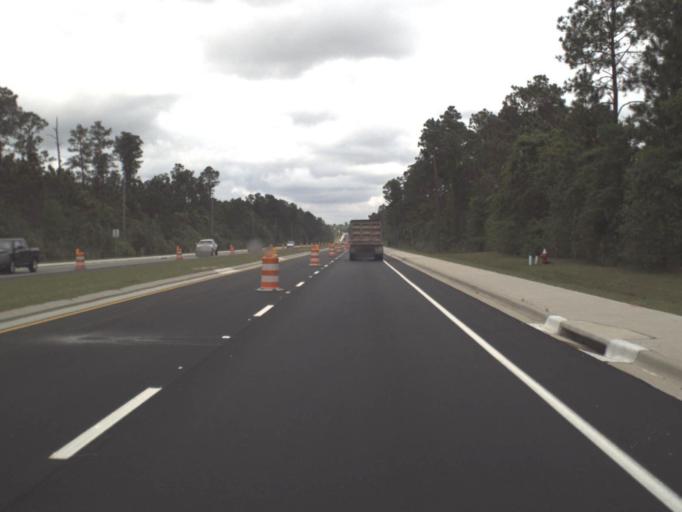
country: US
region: Florida
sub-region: Santa Rosa County
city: Bagdad
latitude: 30.5568
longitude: -87.0870
